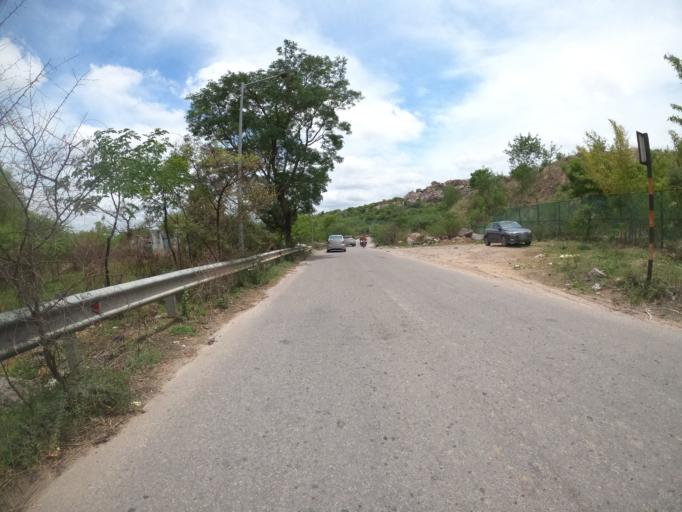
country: IN
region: Telangana
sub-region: Hyderabad
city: Hyderabad
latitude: 17.3151
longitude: 78.3721
